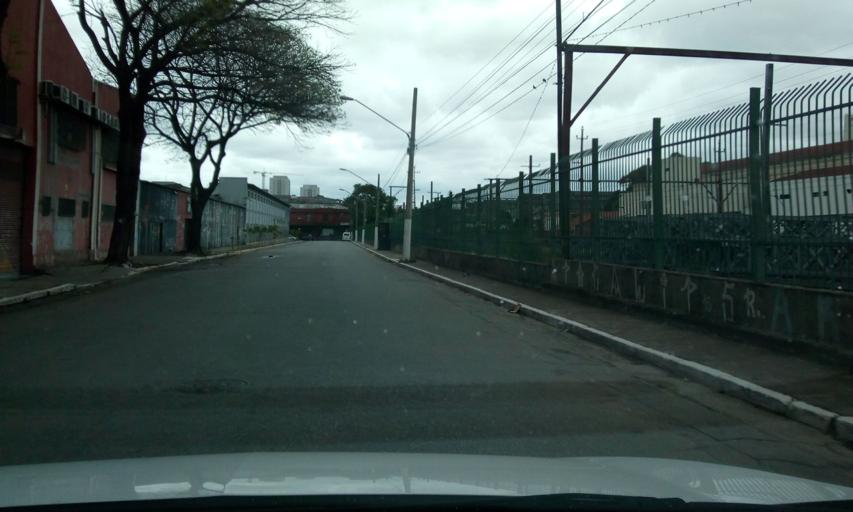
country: BR
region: Sao Paulo
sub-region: Sao Paulo
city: Sao Paulo
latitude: -23.5511
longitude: -46.6131
